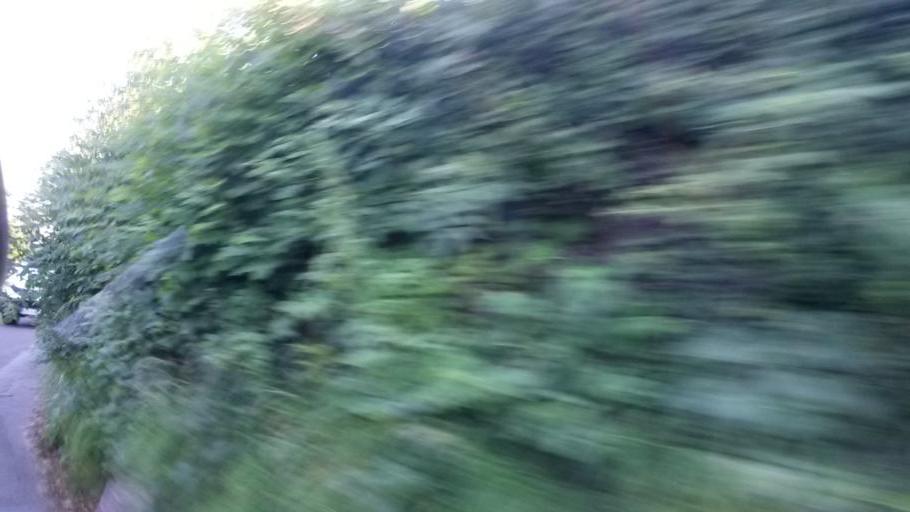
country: IE
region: Leinster
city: Ballymun
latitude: 53.4605
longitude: -6.2973
